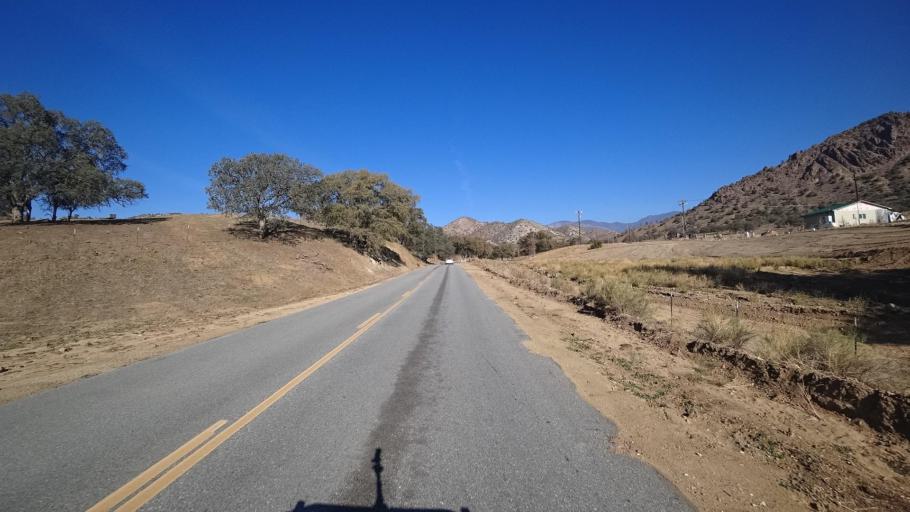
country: US
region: California
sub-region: Kern County
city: Tehachapi
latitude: 35.3252
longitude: -118.3915
